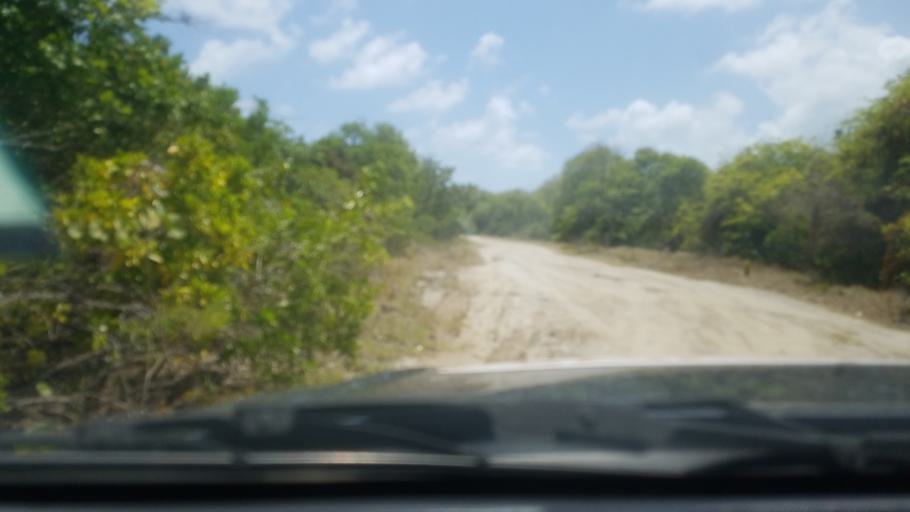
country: LC
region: Vieux-Fort
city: Vieux Fort
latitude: 13.7480
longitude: -60.9348
